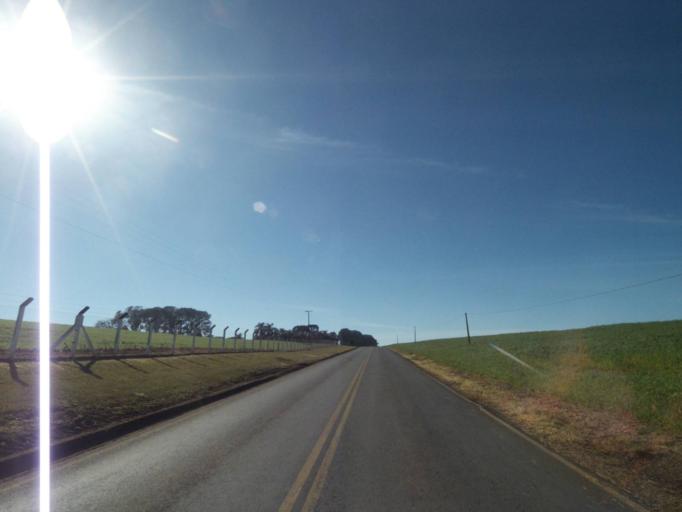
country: BR
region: Parana
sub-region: Tibagi
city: Tibagi
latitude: -24.5255
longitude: -50.3804
